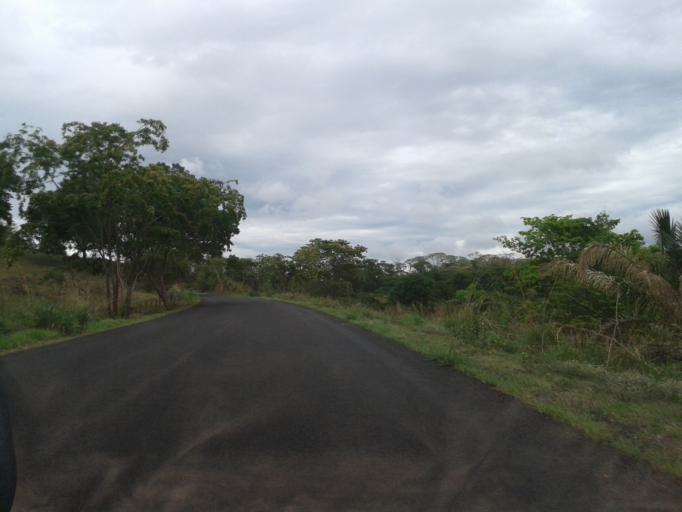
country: BR
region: Goias
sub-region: Caldas Novas
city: Caldas Novas
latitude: -18.0548
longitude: -48.7099
